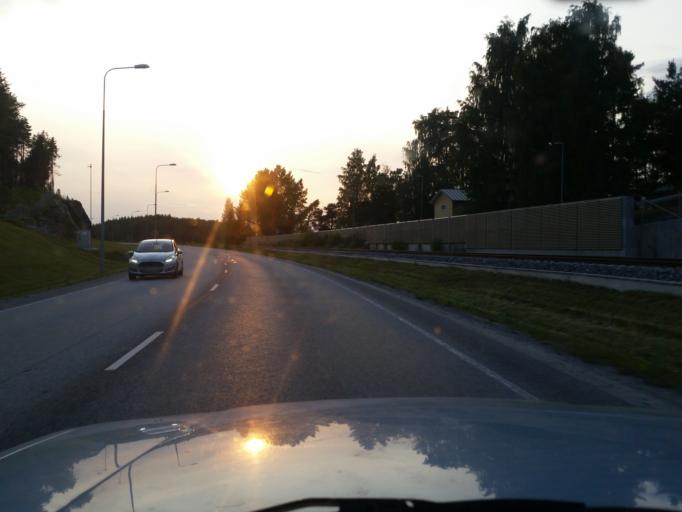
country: FI
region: Southern Savonia
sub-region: Savonlinna
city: Savonlinna
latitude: 61.8794
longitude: 28.8707
